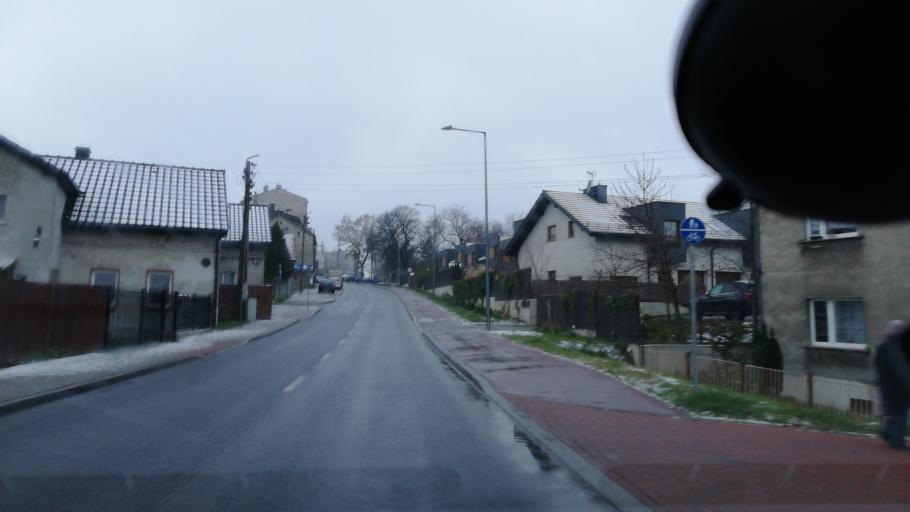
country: PL
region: Silesian Voivodeship
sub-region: Chorzow
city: Chorzow
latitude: 50.2998
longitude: 18.9739
